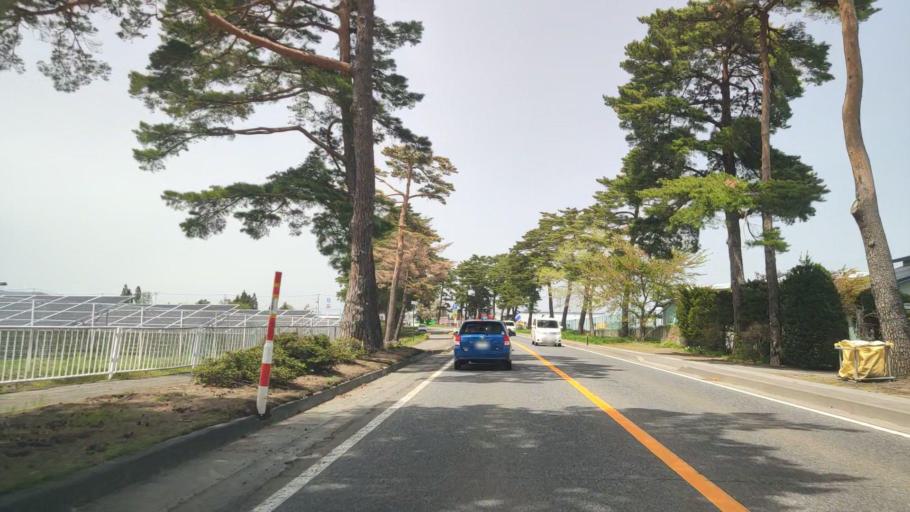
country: JP
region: Aomori
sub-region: Misawa Shi
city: Inuotose
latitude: 40.6711
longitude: 141.1832
